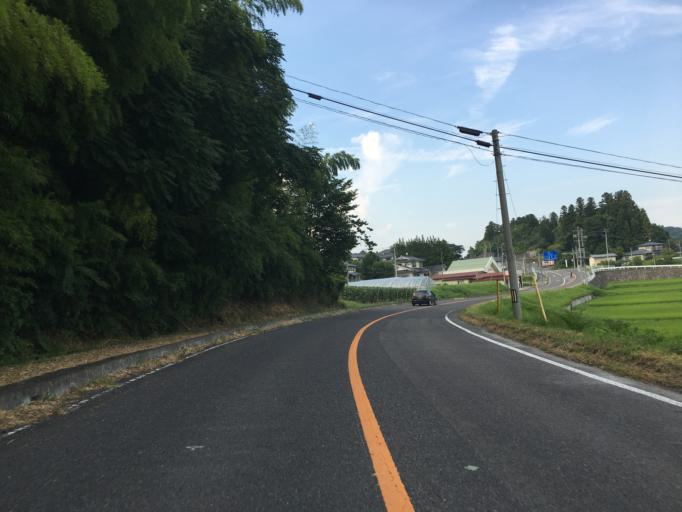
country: JP
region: Fukushima
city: Motomiya
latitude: 37.5233
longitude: 140.4434
